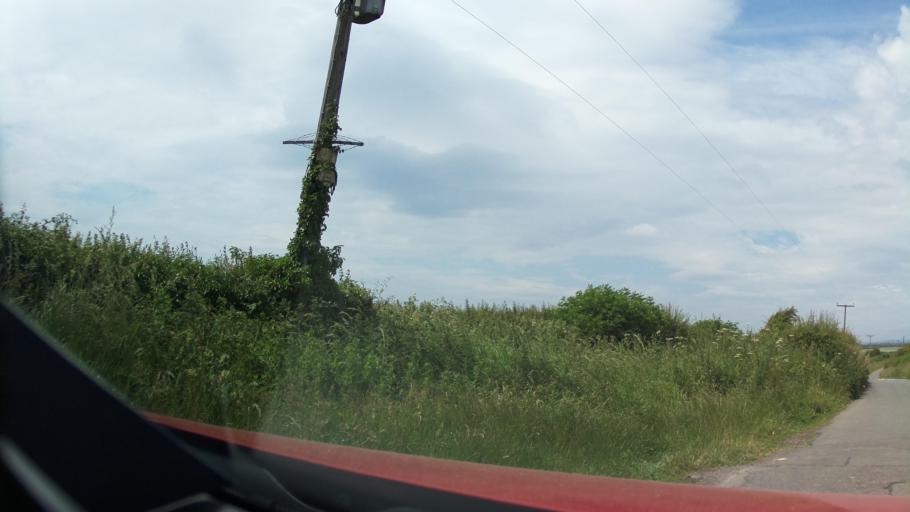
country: GB
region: Wales
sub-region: Vale of Glamorgan
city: Wick
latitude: 51.4347
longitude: -3.5651
